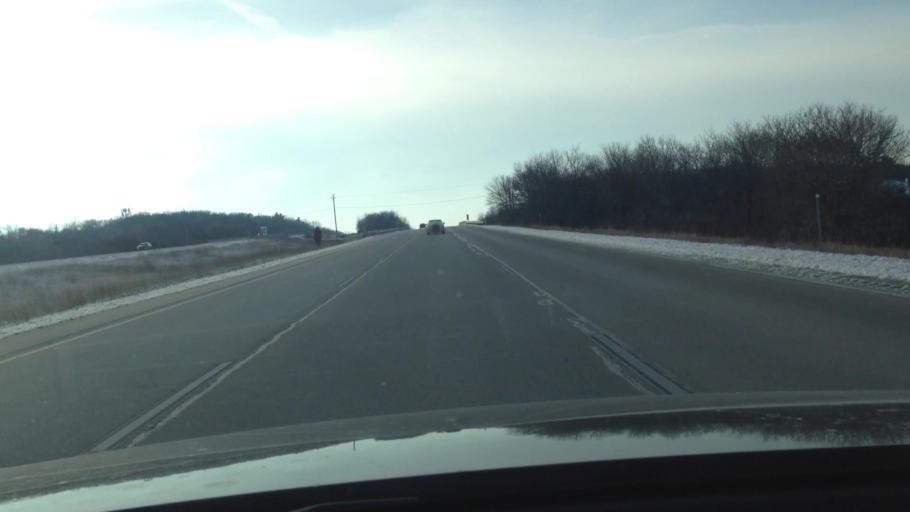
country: US
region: Wisconsin
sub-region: Walworth County
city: East Troy
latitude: 42.7752
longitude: -88.4025
